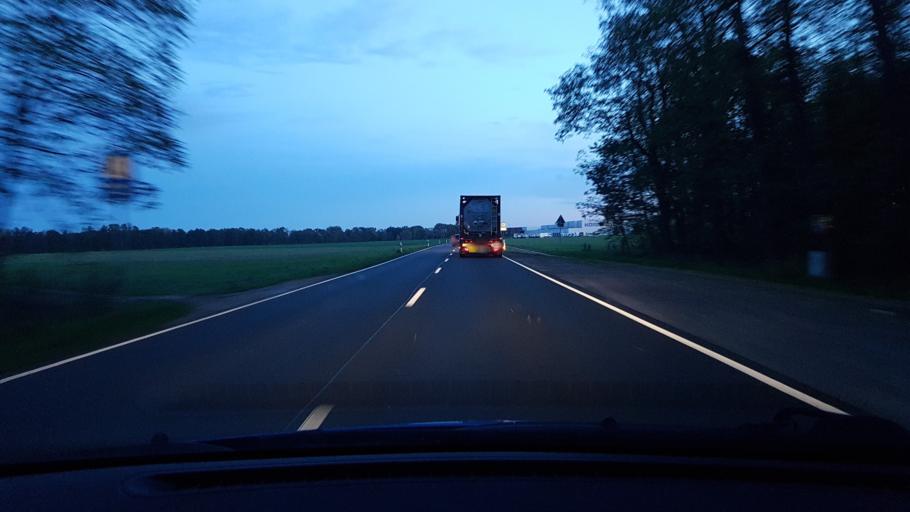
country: DE
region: Saxony-Anhalt
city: Zerbst
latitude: 51.9441
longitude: 12.1161
